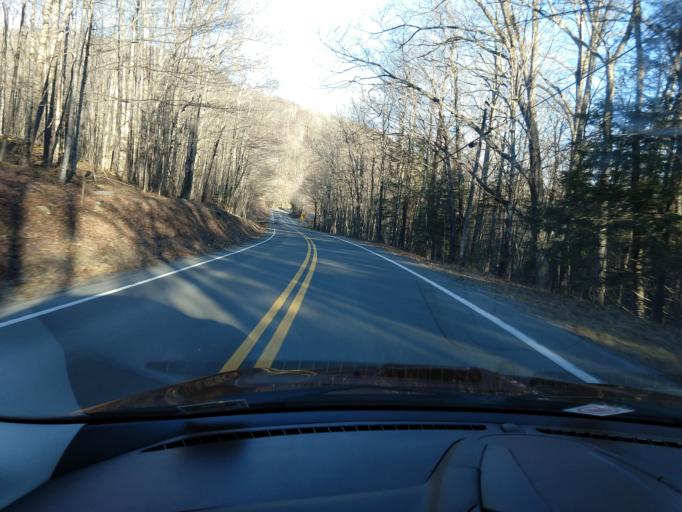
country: US
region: Virginia
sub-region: Highland County
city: Monterey
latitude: 38.5764
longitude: -79.8403
